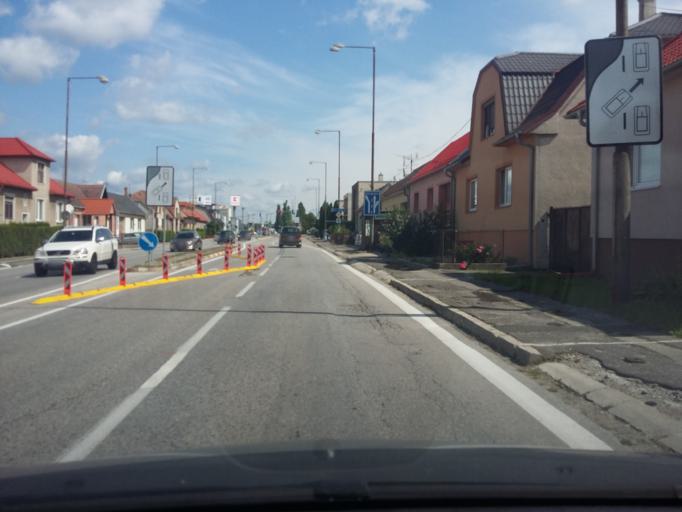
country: SK
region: Bratislavsky
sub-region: Okres Pezinok
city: Pezinok
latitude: 48.2731
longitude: 17.2521
